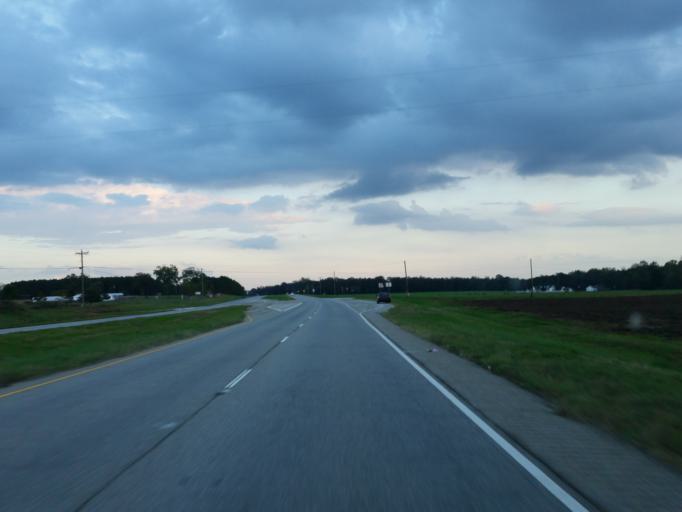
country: US
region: Georgia
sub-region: Pulaski County
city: Hawkinsville
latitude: 32.3176
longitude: -83.5404
